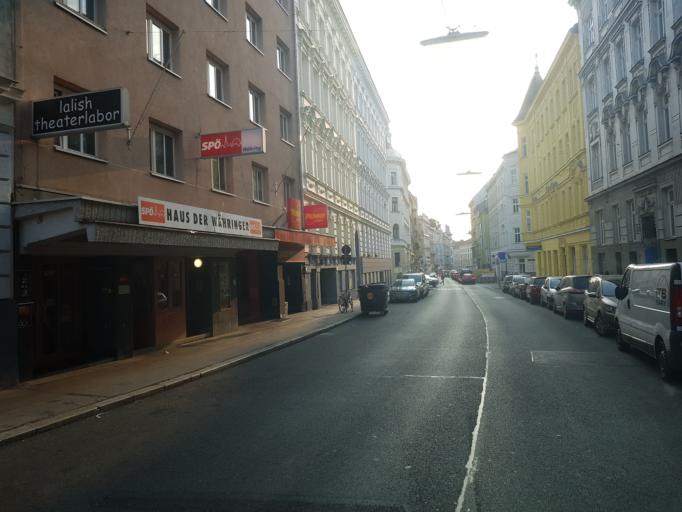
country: AT
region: Vienna
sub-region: Wien Stadt
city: Vienna
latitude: 48.2276
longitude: 16.3400
